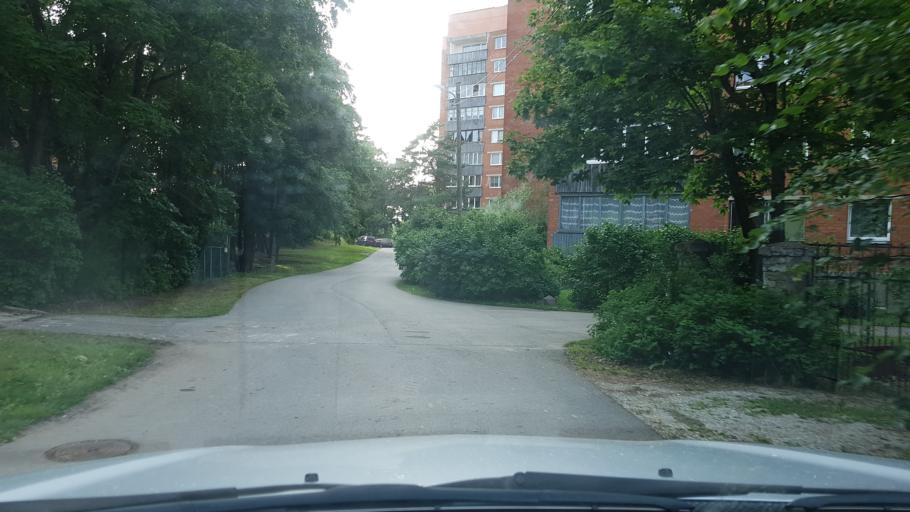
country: EE
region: Ida-Virumaa
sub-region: Narva-Joesuu linn
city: Narva-Joesuu
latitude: 59.4603
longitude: 28.0471
